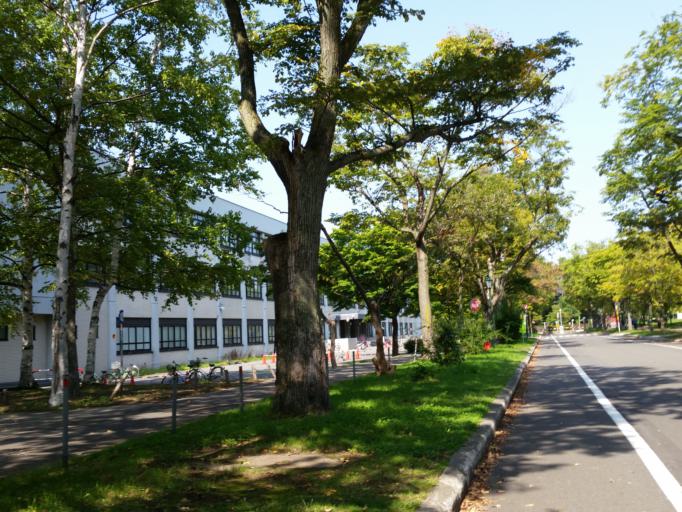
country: JP
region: Hokkaido
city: Sapporo
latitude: 43.0790
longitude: 141.3411
